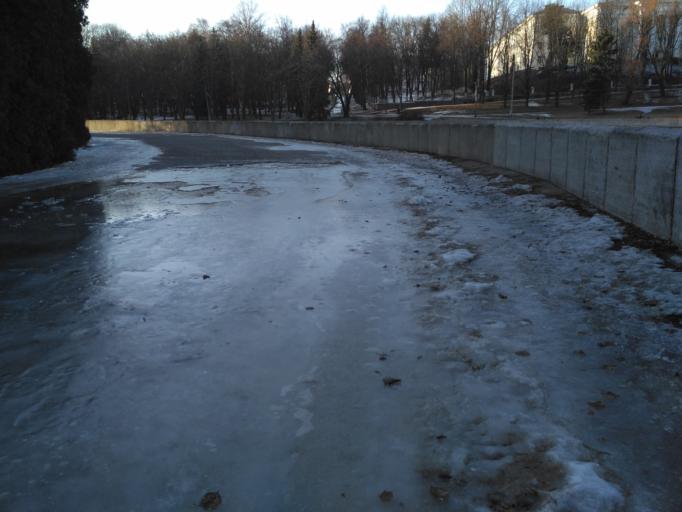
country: BY
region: Minsk
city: Minsk
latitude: 53.9083
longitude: 27.5681
